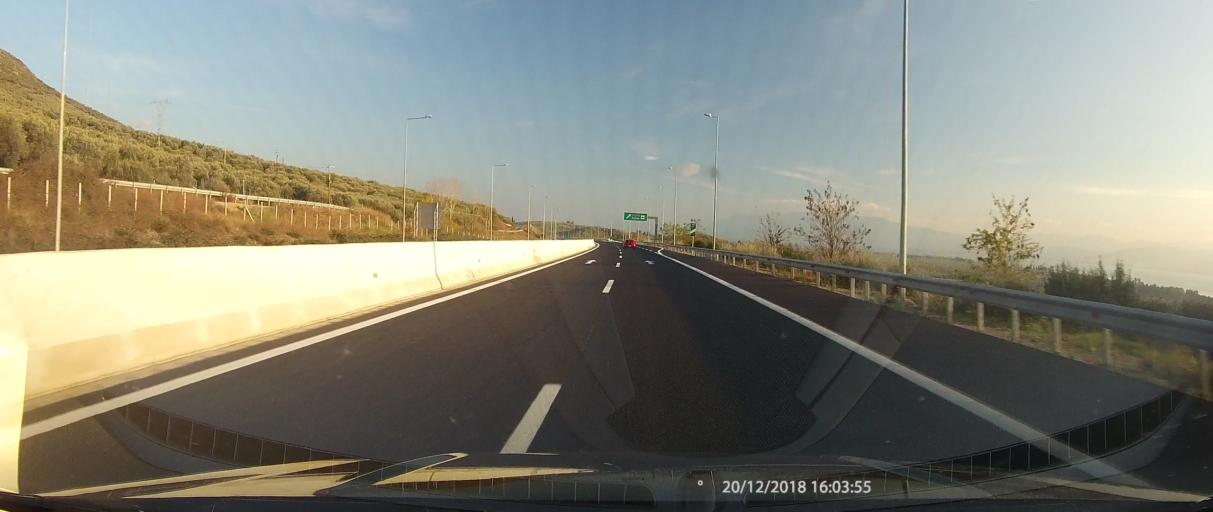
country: GR
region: Central Greece
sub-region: Nomos Fthiotidos
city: Stylida
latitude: 38.9183
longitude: 22.6484
